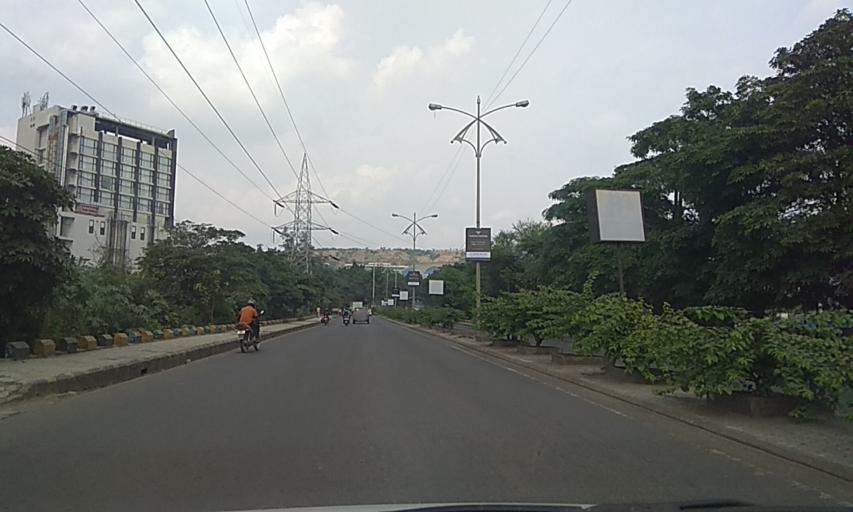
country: IN
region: Maharashtra
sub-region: Pune Division
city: Pimpri
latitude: 18.5920
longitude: 73.7073
